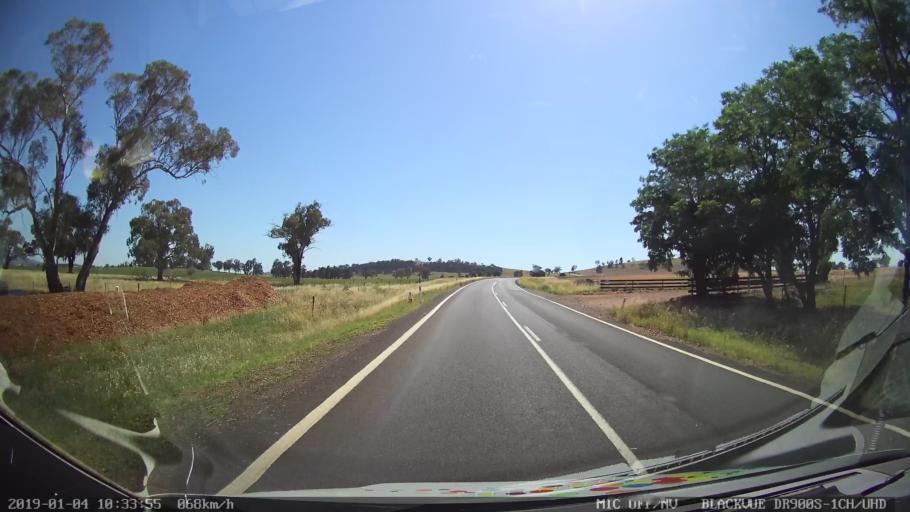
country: AU
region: New South Wales
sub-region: Cabonne
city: Canowindra
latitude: -33.3162
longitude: 148.6563
